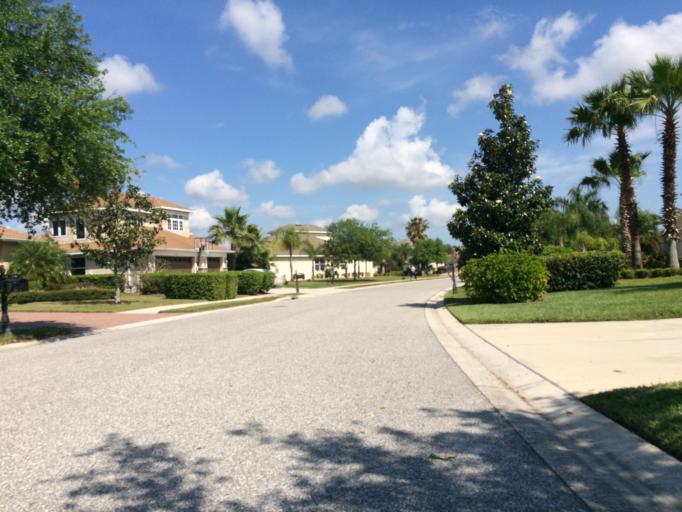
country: US
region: Florida
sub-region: Manatee County
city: Ellenton
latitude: 27.5032
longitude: -82.4215
